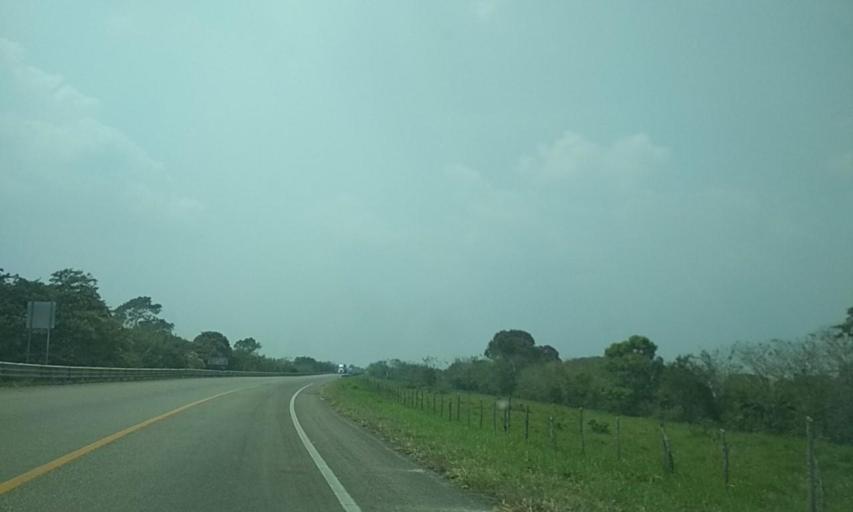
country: MX
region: Tabasco
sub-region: Huimanguillo
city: Francisco Rueda
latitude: 17.7736
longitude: -94.0465
